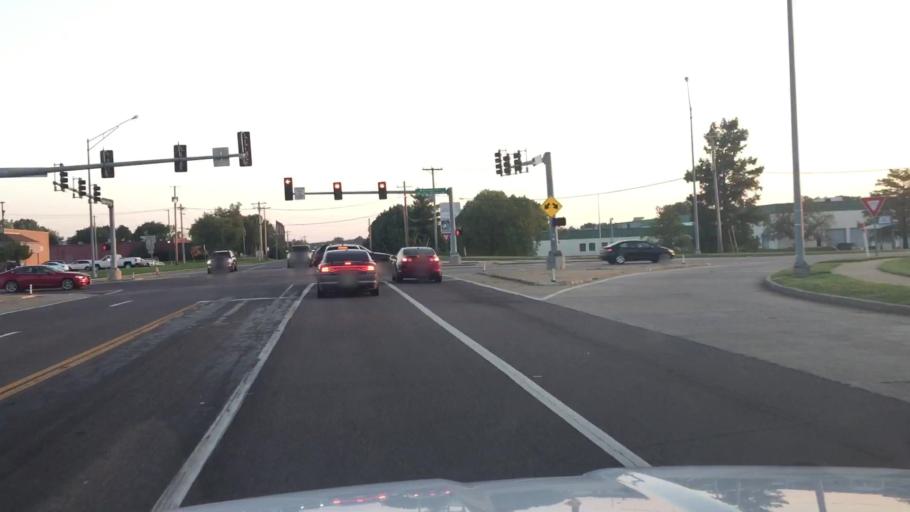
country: US
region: Missouri
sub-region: Jefferson County
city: Arnold
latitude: 38.4652
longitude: -90.3568
